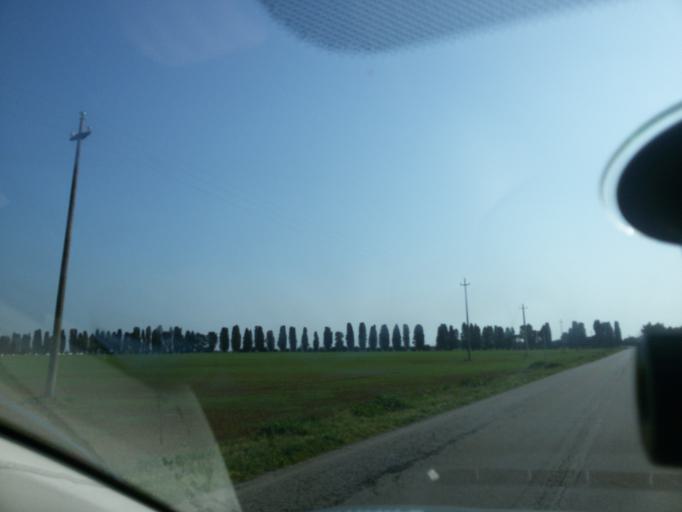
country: IT
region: Apulia
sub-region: Provincia di Brindisi
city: Mesagne
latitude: 40.5986
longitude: 17.8170
